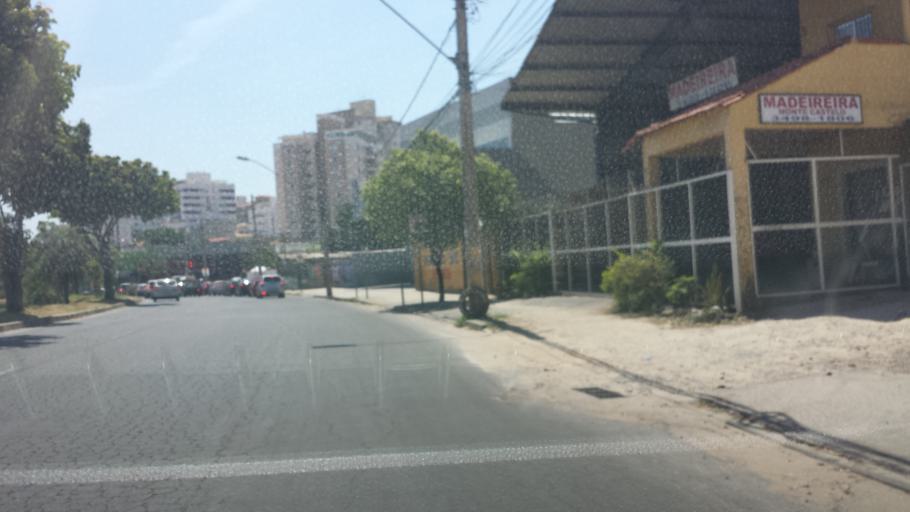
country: BR
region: Minas Gerais
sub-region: Belo Horizonte
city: Belo Horizonte
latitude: -19.8762
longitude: -43.9921
